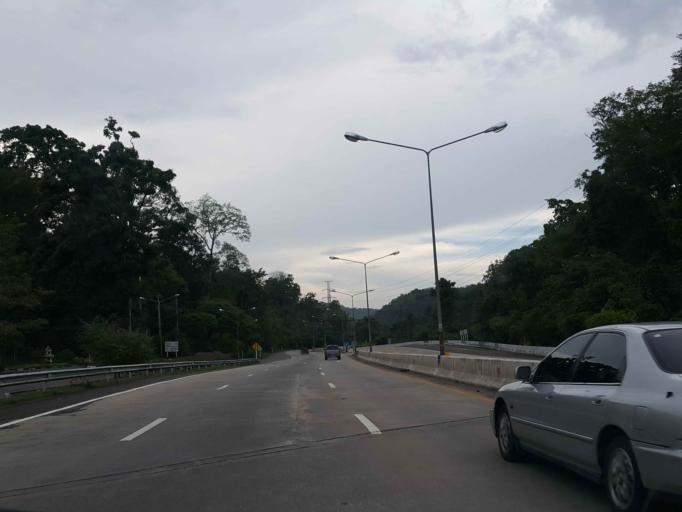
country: TH
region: Lamphun
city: Mae Tha
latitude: 18.3919
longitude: 99.2167
